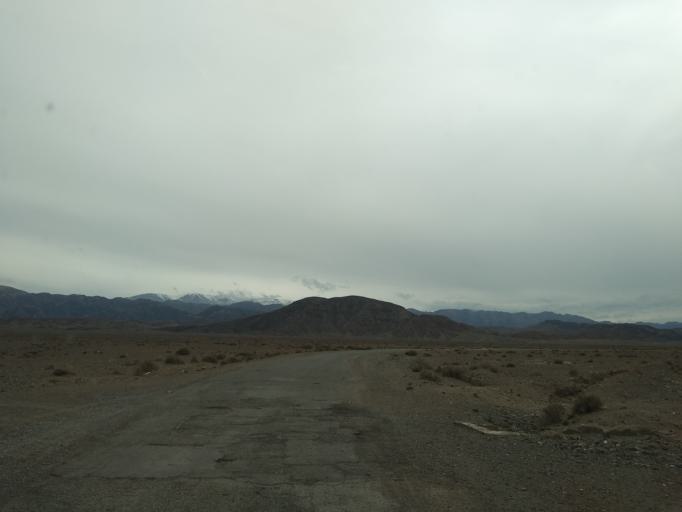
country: KG
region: Ysyk-Koel
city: Balykchy
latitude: 42.3196
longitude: 76.2339
